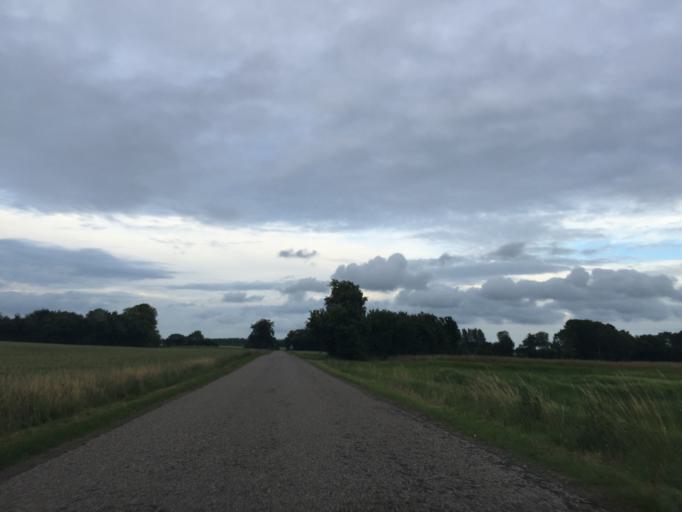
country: DK
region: Central Jutland
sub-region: Silkeborg Kommune
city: Silkeborg
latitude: 56.2445
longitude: 9.5093
